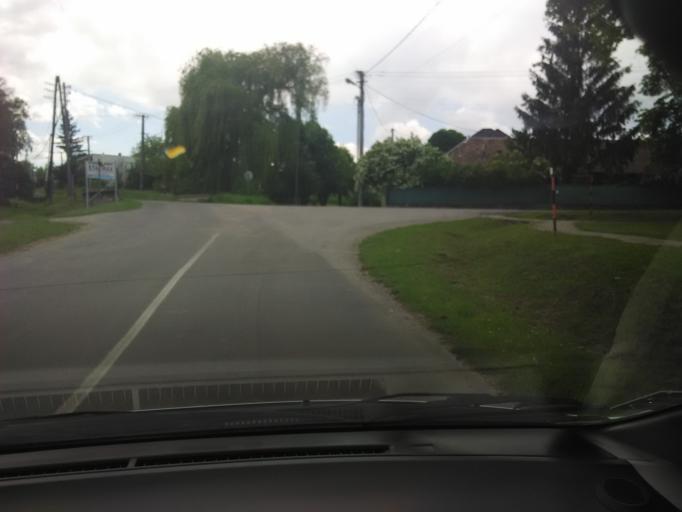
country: SK
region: Nitriansky
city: Levice
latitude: 48.1281
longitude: 18.4617
